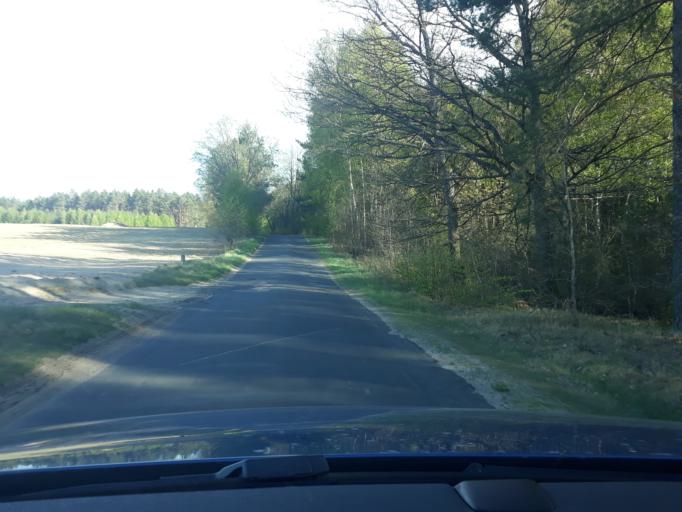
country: PL
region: Pomeranian Voivodeship
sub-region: Powiat czluchowski
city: Przechlewo
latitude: 53.8616
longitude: 17.3420
